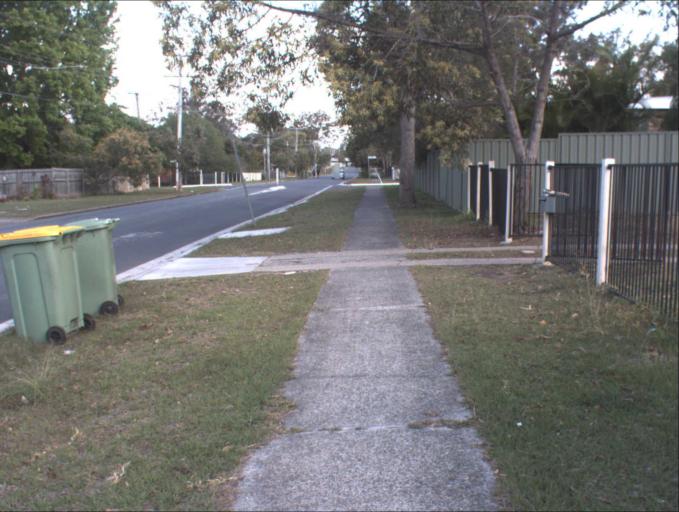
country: AU
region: Queensland
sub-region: Logan
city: Waterford West
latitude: -27.6717
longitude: 153.1250
